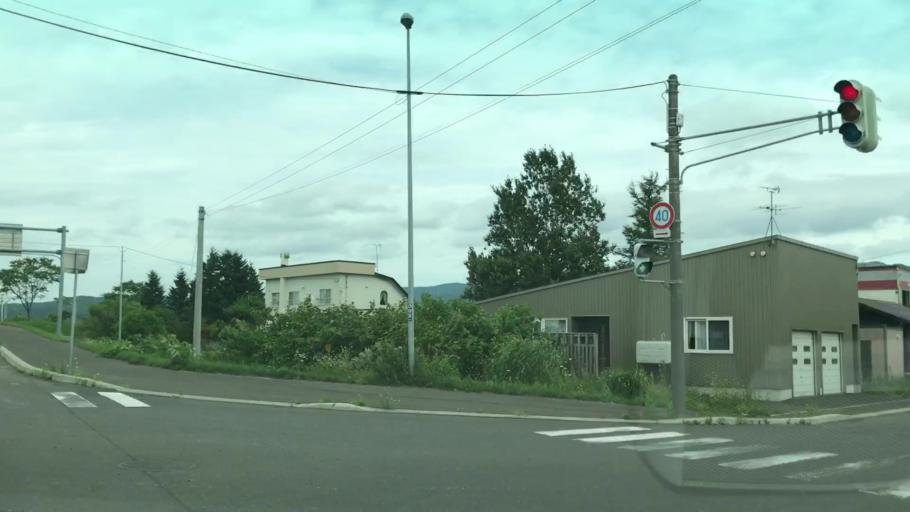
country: JP
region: Hokkaido
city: Iwanai
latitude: 43.0164
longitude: 140.5679
